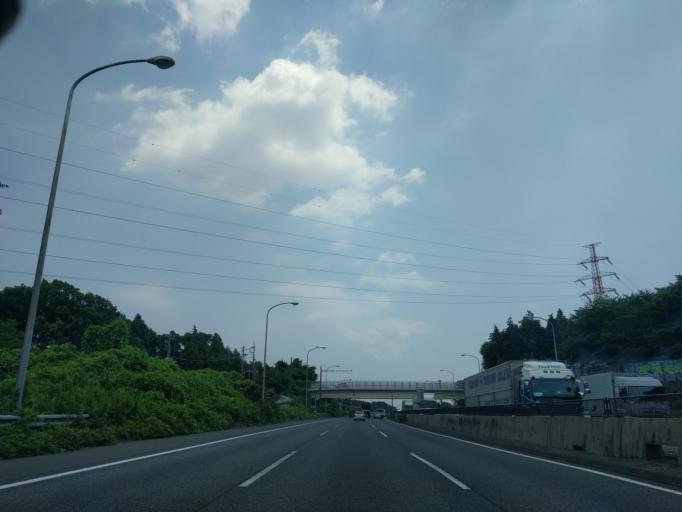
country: JP
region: Kanagawa
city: Minami-rinkan
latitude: 35.4911
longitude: 139.5044
